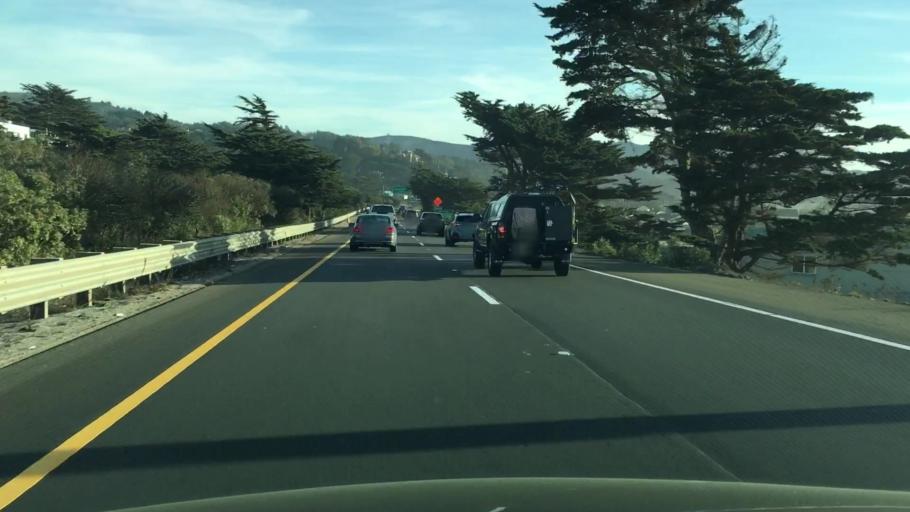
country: US
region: California
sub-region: San Mateo County
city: Pacifica
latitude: 37.6425
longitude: -122.4917
